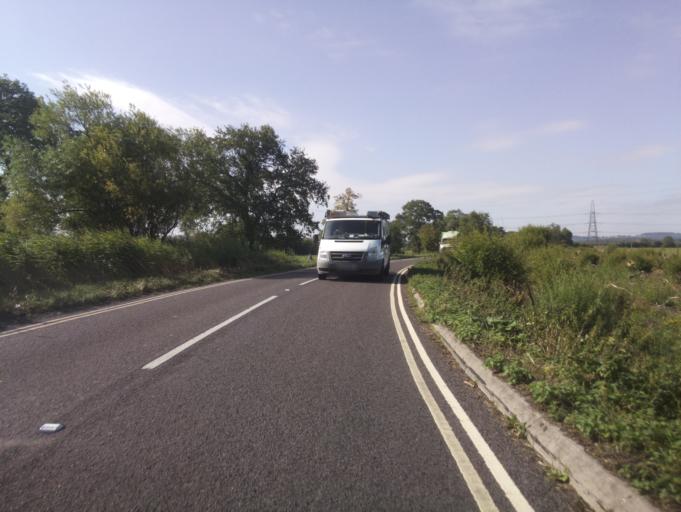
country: GB
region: England
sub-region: Oxfordshire
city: Faringdon
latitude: 51.6919
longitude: -1.5878
